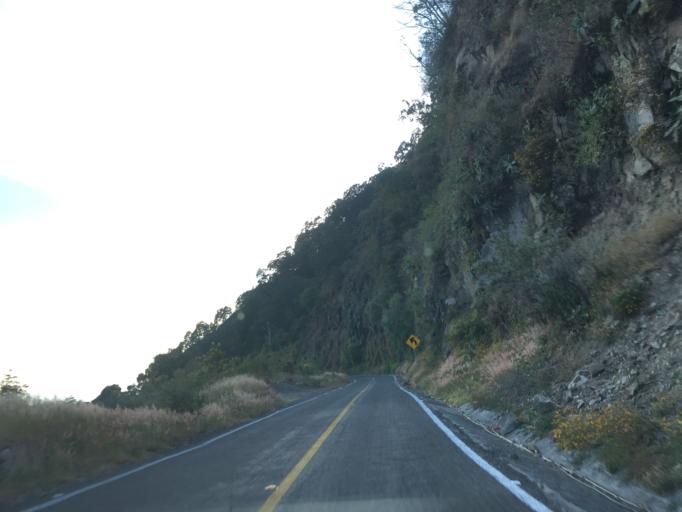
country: MX
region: Michoacan
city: Tzitzio
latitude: 19.6620
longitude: -100.9221
